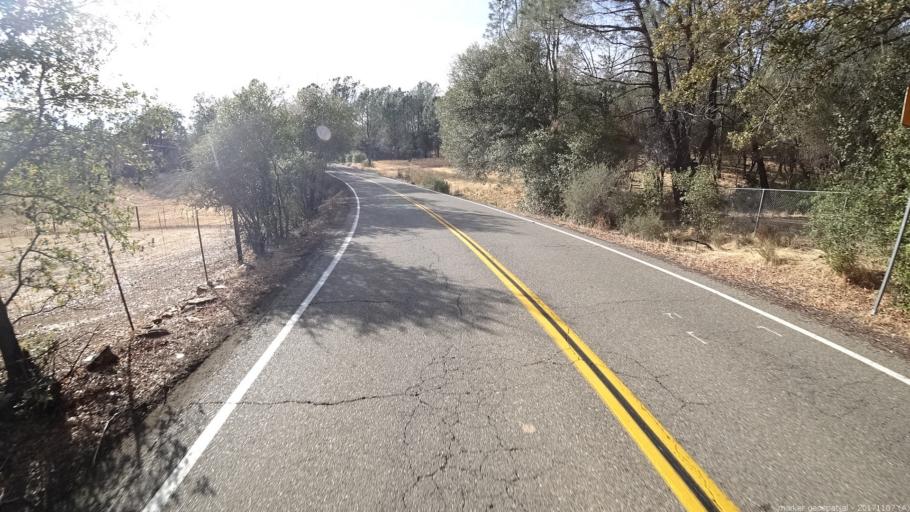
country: US
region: California
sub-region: Shasta County
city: Shasta
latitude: 40.5200
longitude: -122.4983
